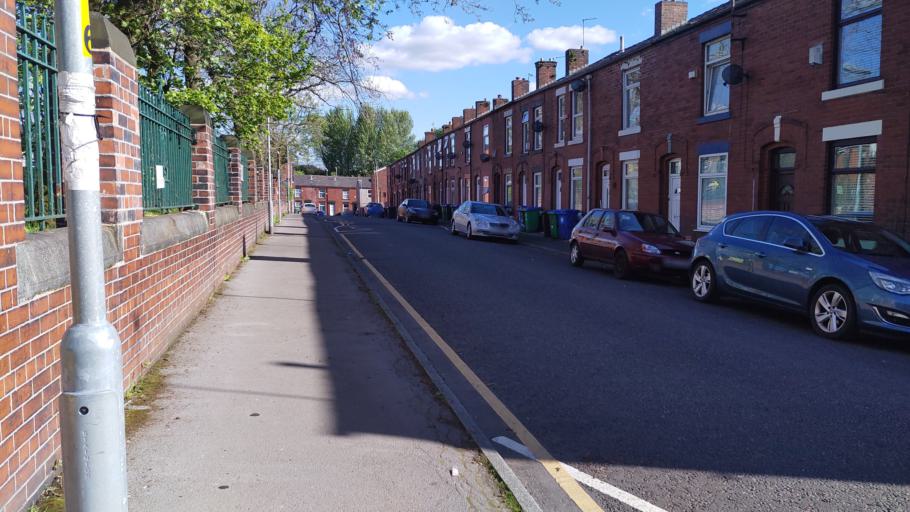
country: GB
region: England
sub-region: Borough of Rochdale
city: Rochdale
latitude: 53.6057
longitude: -2.1723
